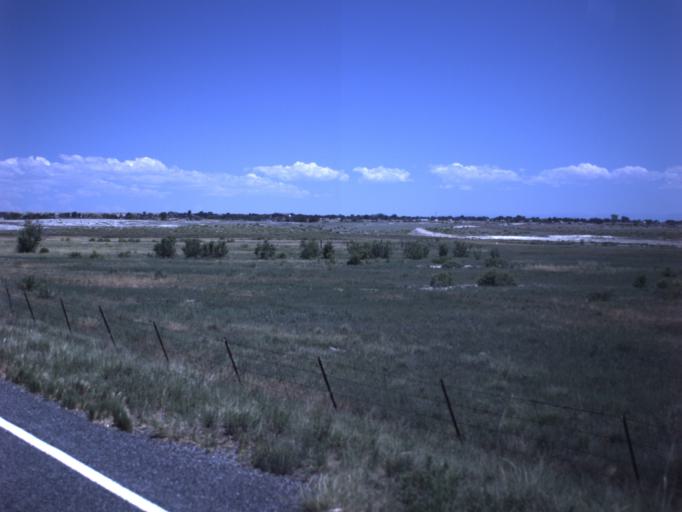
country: US
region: Utah
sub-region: Emery County
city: Orangeville
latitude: 39.1948
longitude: -111.0478
